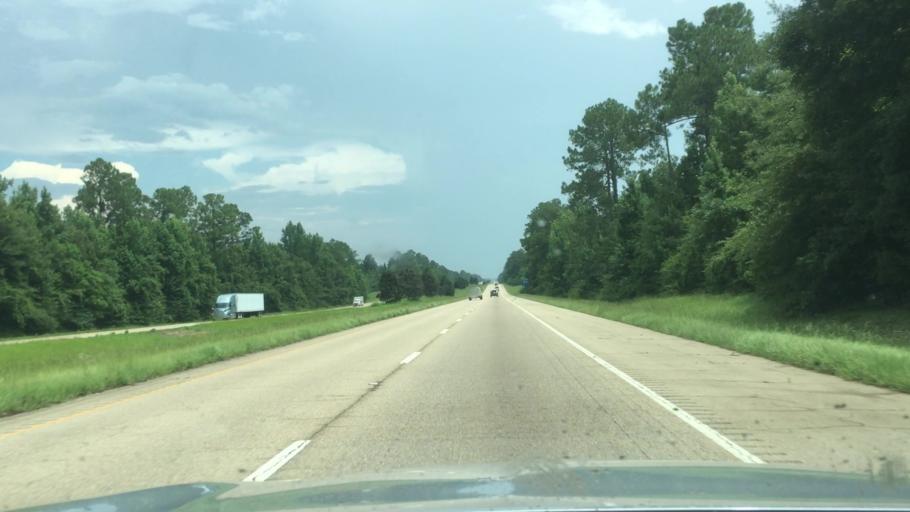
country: US
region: Mississippi
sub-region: Lamar County
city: Lumberton
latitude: 30.9343
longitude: -89.4524
